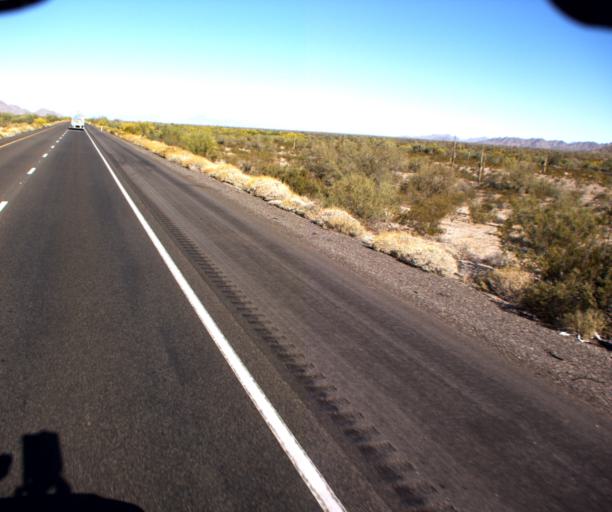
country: US
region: Arizona
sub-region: Maricopa County
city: Gila Bend
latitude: 32.8797
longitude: -112.4546
